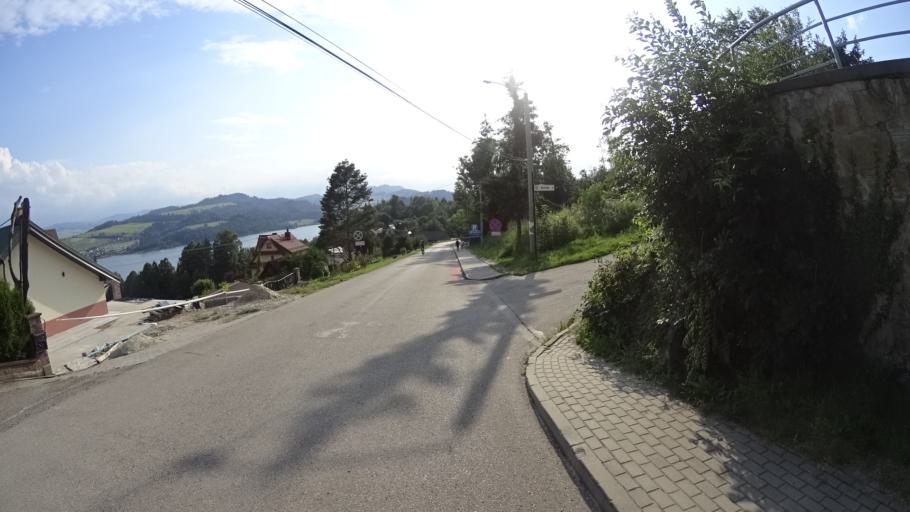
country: PL
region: Lesser Poland Voivodeship
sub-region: Powiat nowotarski
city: Krosnica
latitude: 49.4360
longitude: 20.3230
